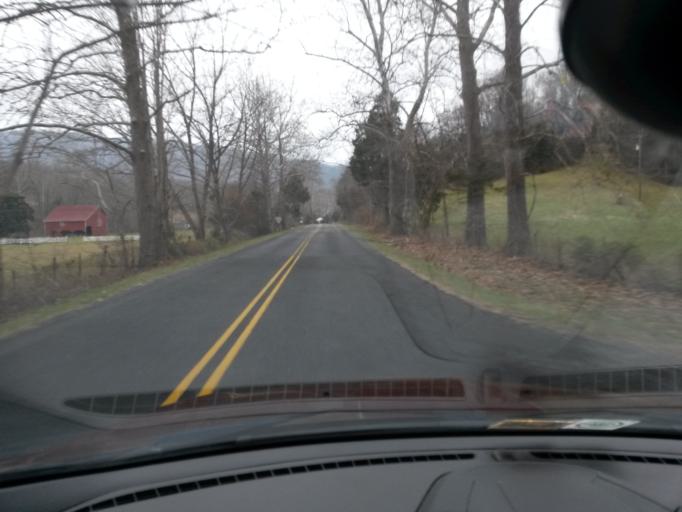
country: US
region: Virginia
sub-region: City of Lexington
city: Lexington
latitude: 37.8716
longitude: -79.5559
